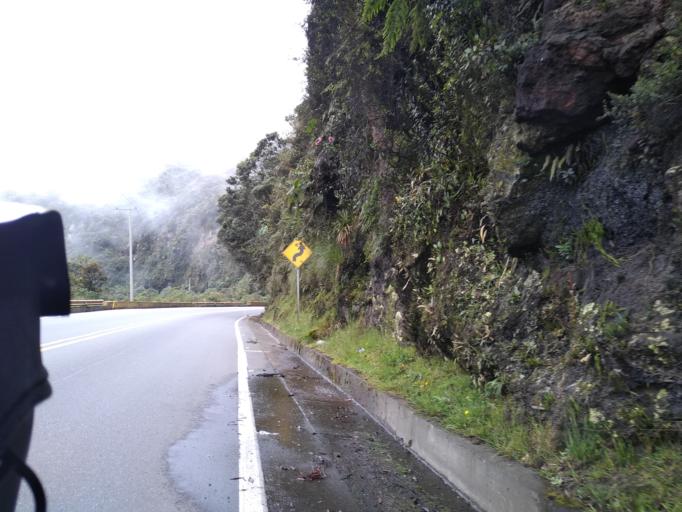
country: CO
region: Tolima
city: Herveo
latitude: 5.0804
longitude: -75.2800
